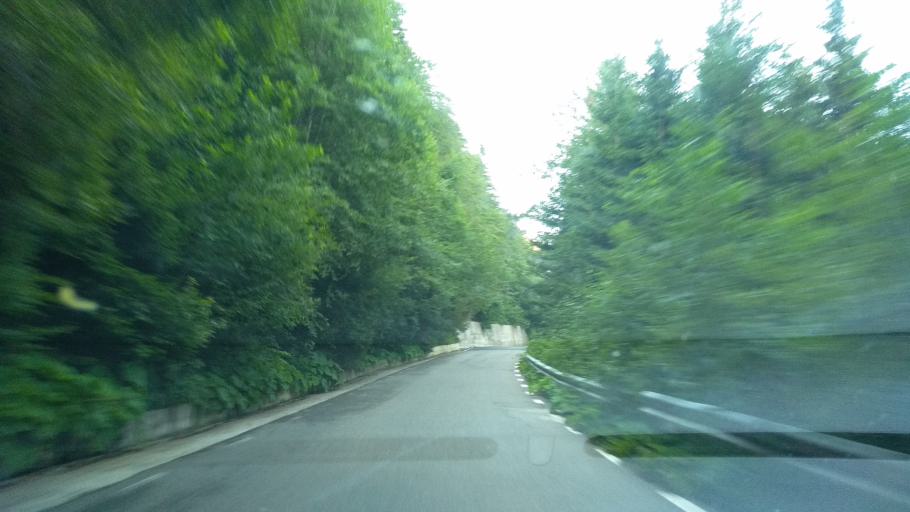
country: RO
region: Prahova
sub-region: Oras Sinaia
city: Sinaia
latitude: 45.3225
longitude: 25.4958
